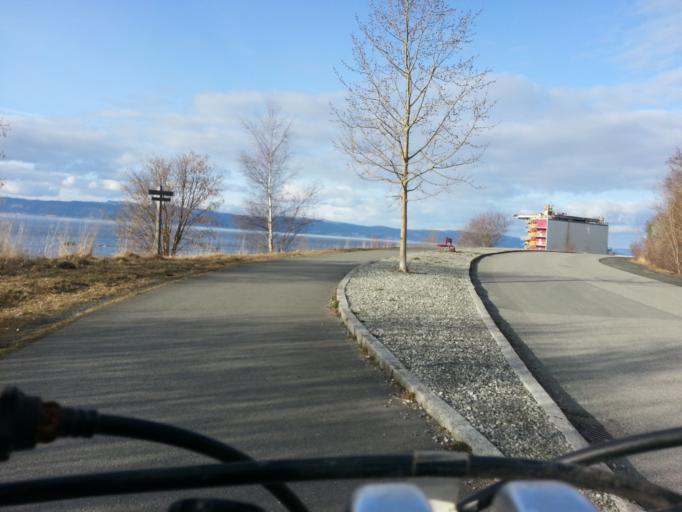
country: NO
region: Sor-Trondelag
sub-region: Trondheim
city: Trondheim
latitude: 63.4456
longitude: 10.4215
